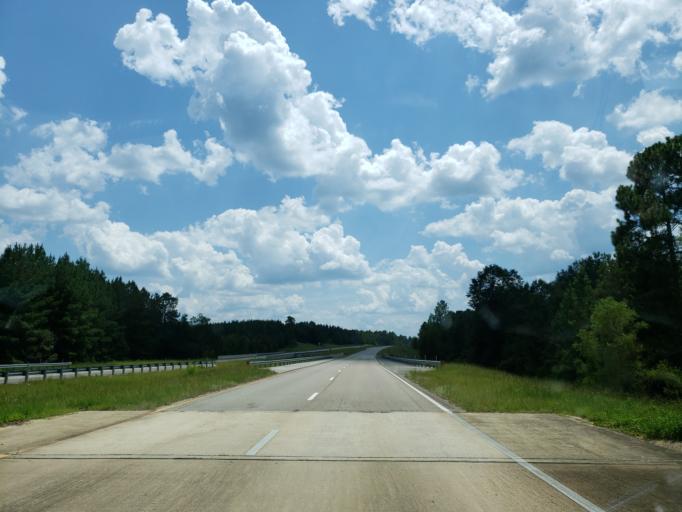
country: US
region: Mississippi
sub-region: Greene County
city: Leakesville
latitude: 31.1512
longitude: -88.5004
